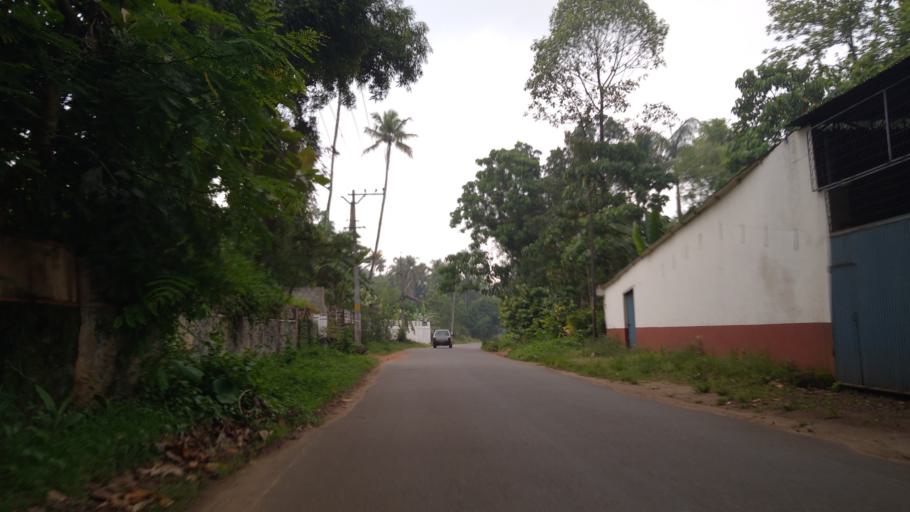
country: IN
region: Kerala
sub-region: Ernakulam
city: Perumbavoor
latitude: 10.0873
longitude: 76.5131
